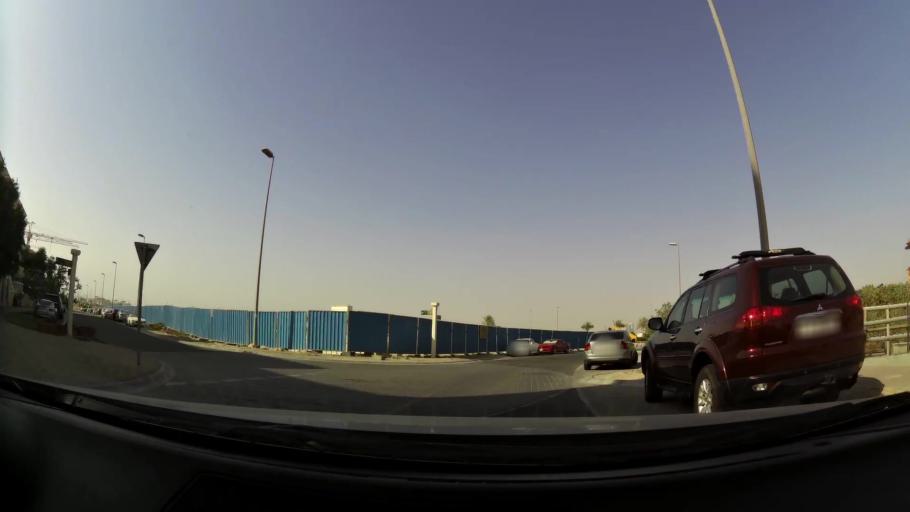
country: AE
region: Dubai
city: Dubai
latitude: 25.0633
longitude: 55.2174
